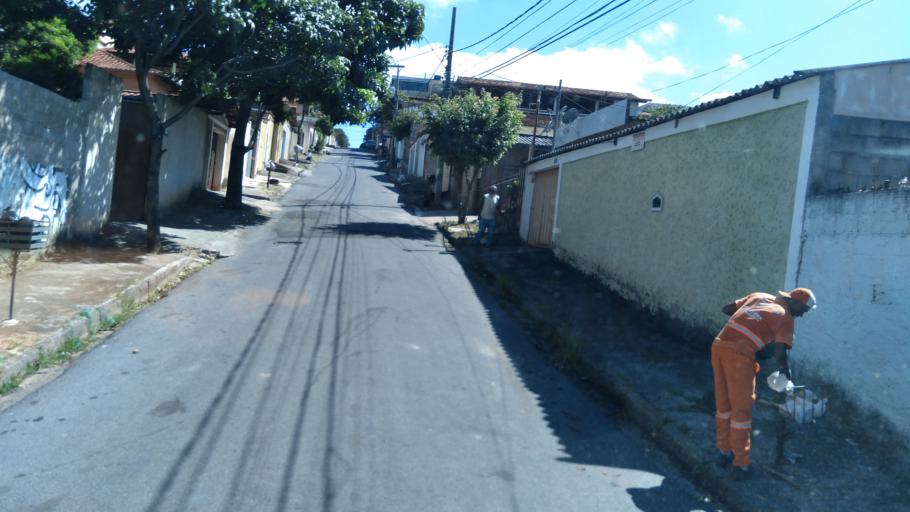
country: BR
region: Minas Gerais
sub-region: Belo Horizonte
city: Belo Horizonte
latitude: -19.8802
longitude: -43.9231
